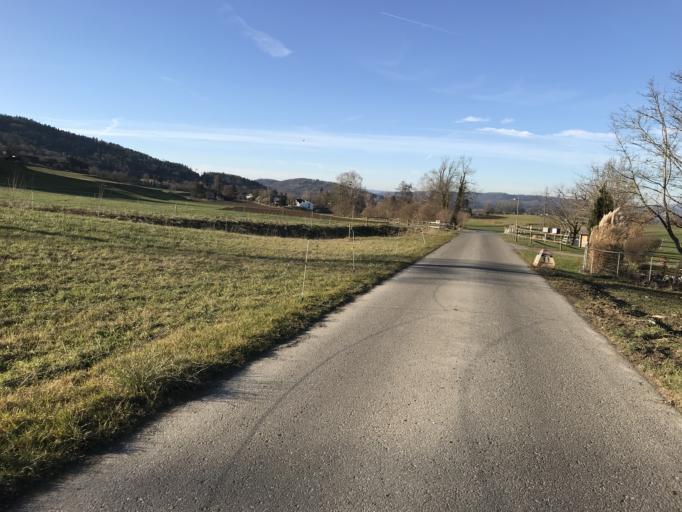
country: CH
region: Thurgau
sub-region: Frauenfeld District
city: Wagenhausen
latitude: 47.6467
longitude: 8.8480
